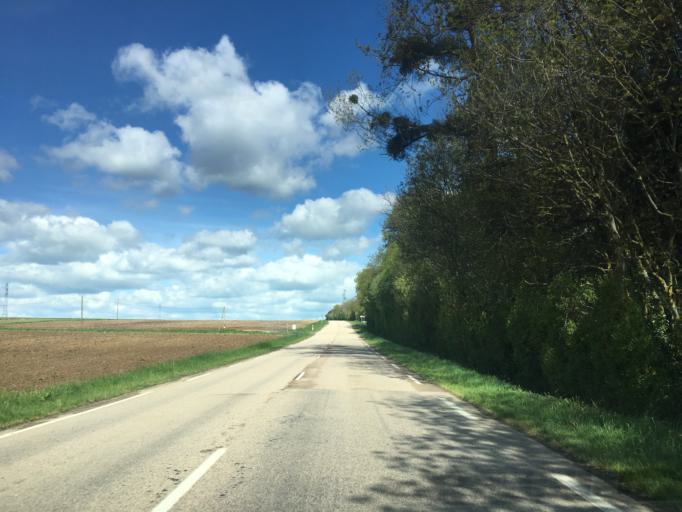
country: FR
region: Lower Normandy
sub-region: Departement de l'Orne
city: Rai
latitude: 48.8038
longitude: 0.5859
